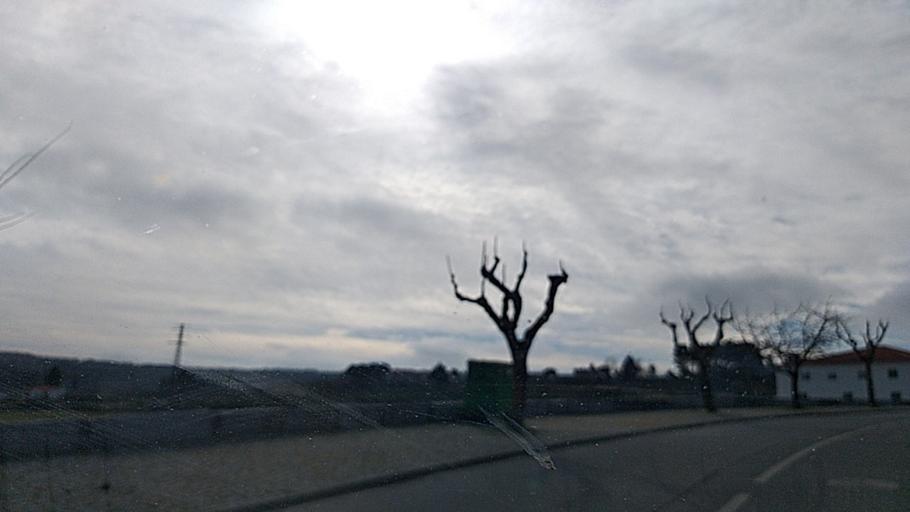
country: PT
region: Guarda
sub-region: Fornos de Algodres
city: Fornos de Algodres
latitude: 40.6792
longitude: -7.5302
